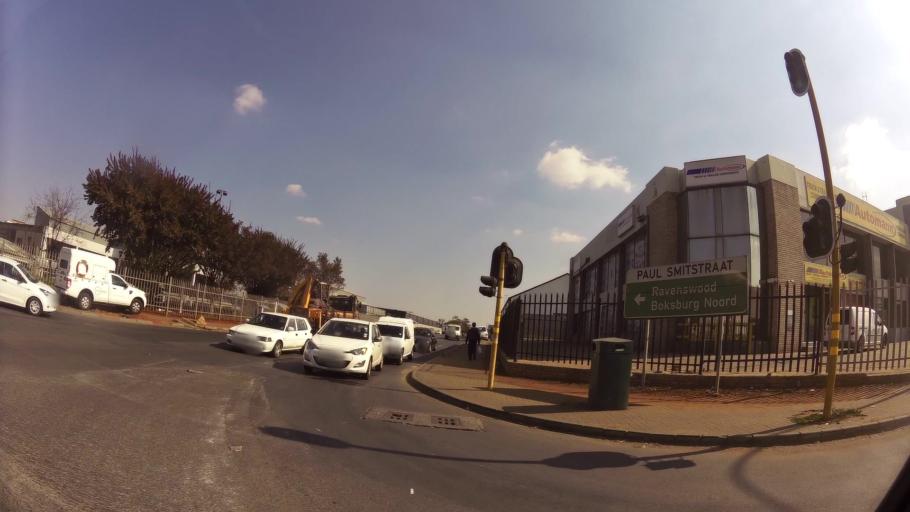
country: ZA
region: Gauteng
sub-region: Ekurhuleni Metropolitan Municipality
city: Boksburg
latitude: -26.2004
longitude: 28.2835
